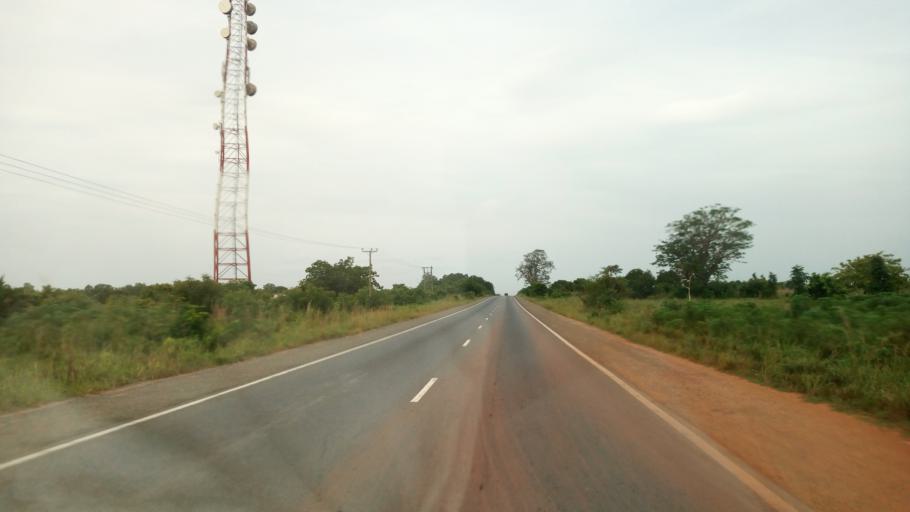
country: GH
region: Volta
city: Keta
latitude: 6.0627
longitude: 1.0036
